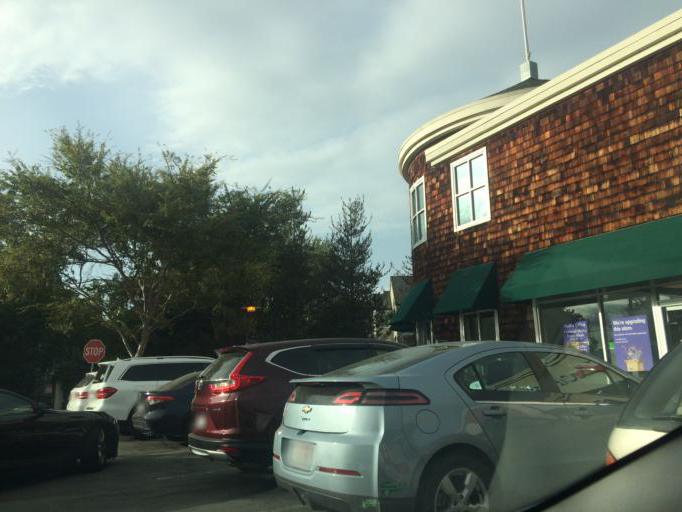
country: US
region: California
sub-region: Santa Clara County
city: San Jose
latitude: 37.3837
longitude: -121.8951
